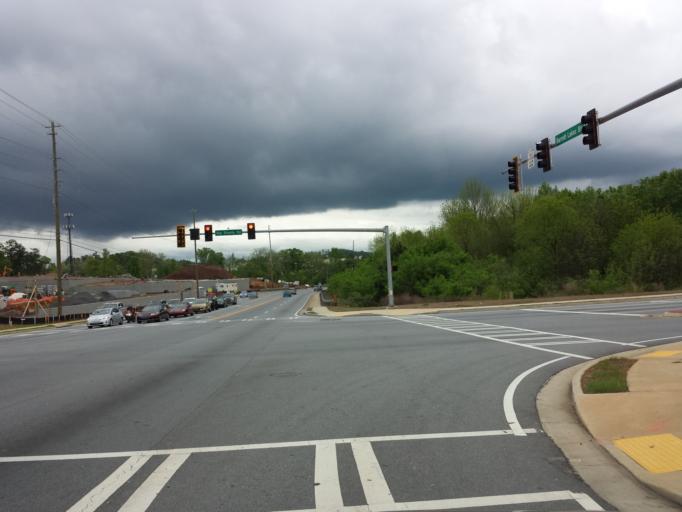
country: US
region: Georgia
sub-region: Cobb County
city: Kennesaw
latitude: 34.0254
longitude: -84.5754
